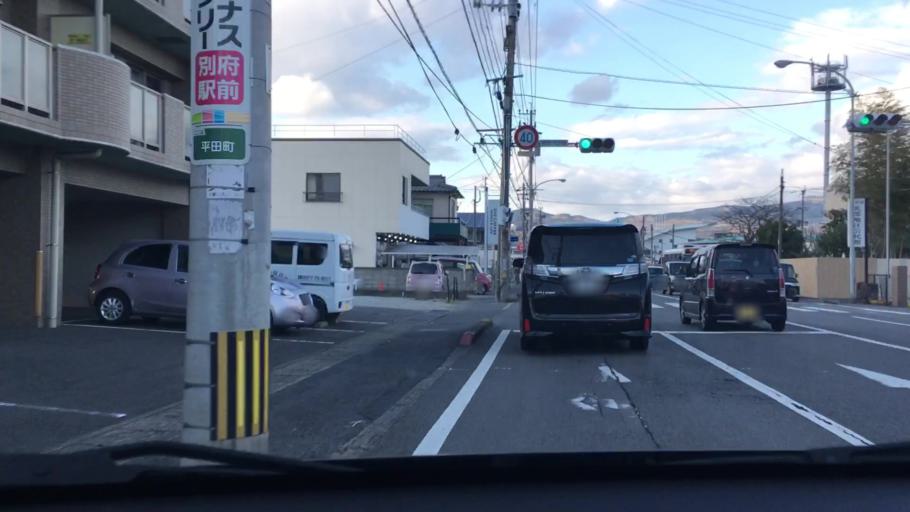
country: JP
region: Oita
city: Beppu
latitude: 33.3194
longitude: 131.4990
